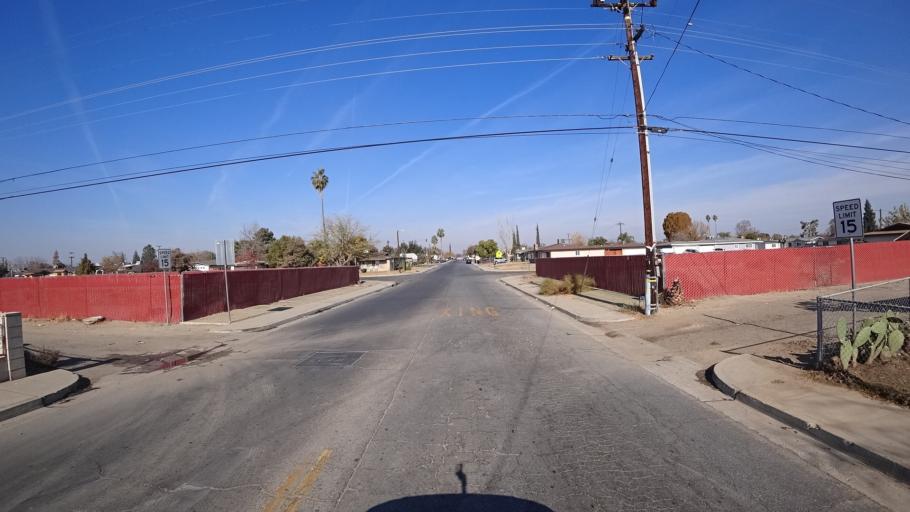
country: US
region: California
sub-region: Kern County
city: Greenfield
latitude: 35.3180
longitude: -119.0163
